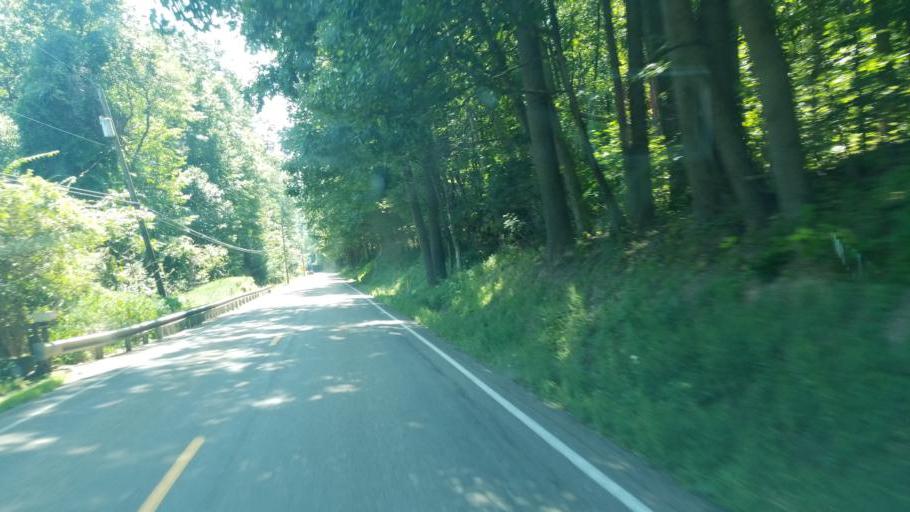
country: US
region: Pennsylvania
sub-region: Clarion County
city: Knox
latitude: 41.1528
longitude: -79.6846
